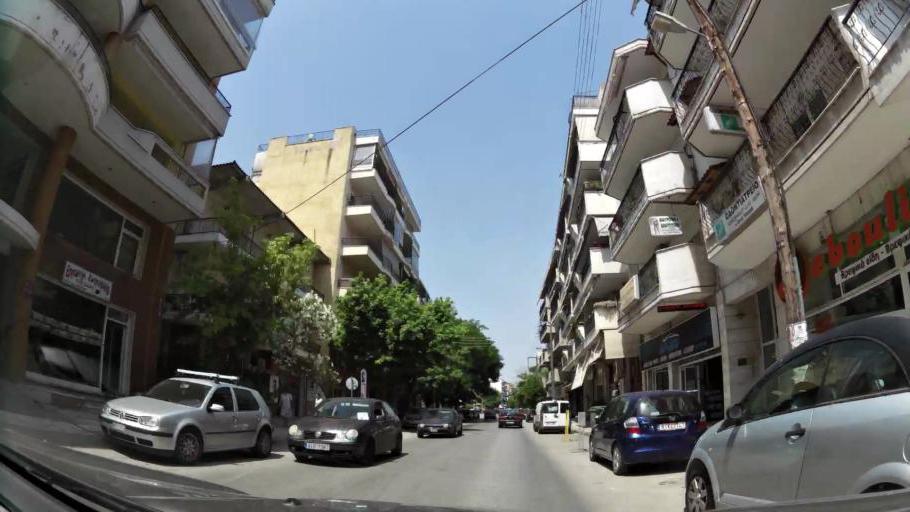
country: GR
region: Central Macedonia
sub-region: Nomos Thessalonikis
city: Evosmos
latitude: 40.6706
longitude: 22.9036
